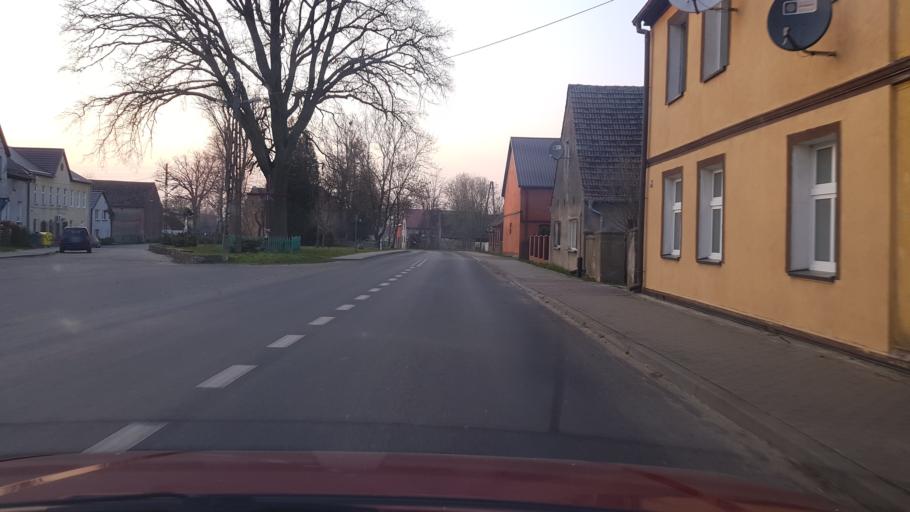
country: PL
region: West Pomeranian Voivodeship
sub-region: Powiat lobeski
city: Radowo Male
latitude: 53.6640
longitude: 15.4501
